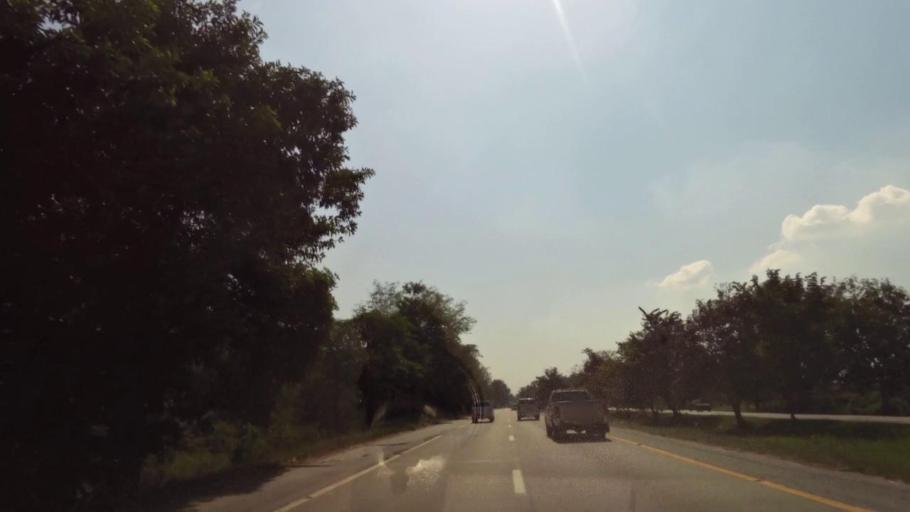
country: TH
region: Phichit
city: Wachira Barami
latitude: 16.5713
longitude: 100.1485
